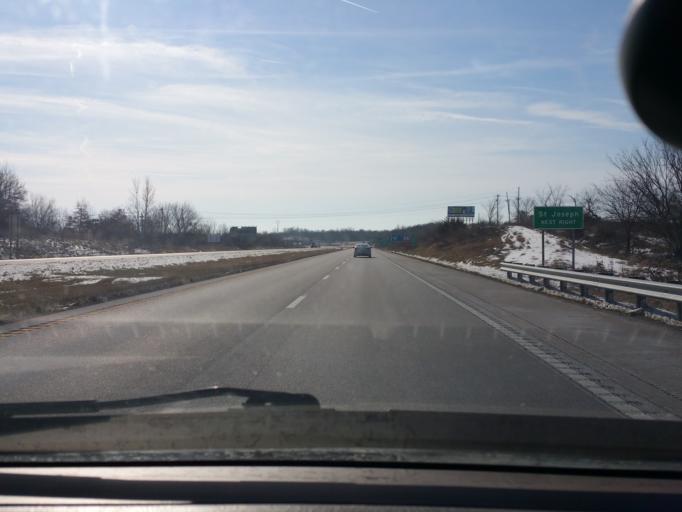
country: US
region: Missouri
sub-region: Clinton County
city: Cameron
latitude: 39.7628
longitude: -94.2172
